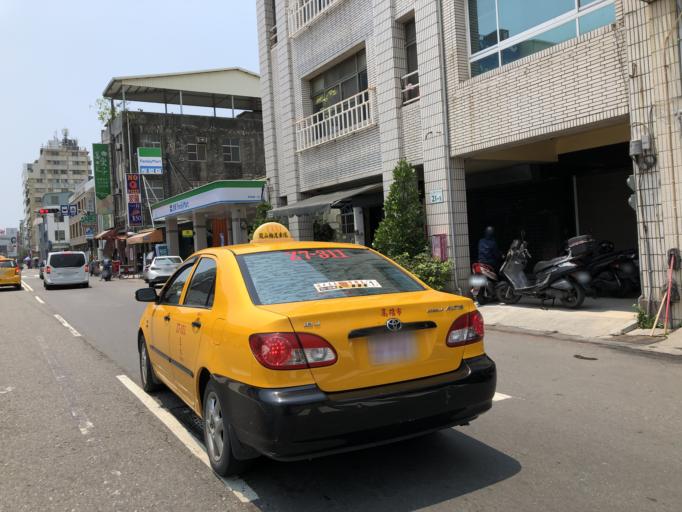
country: TW
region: Kaohsiung
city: Kaohsiung
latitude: 22.6223
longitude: 120.2744
